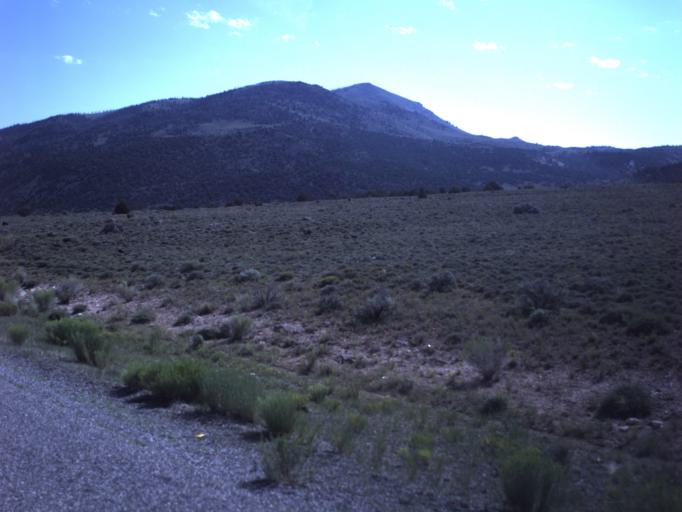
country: US
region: Utah
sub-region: Wayne County
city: Loa
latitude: 38.5018
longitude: -111.5331
